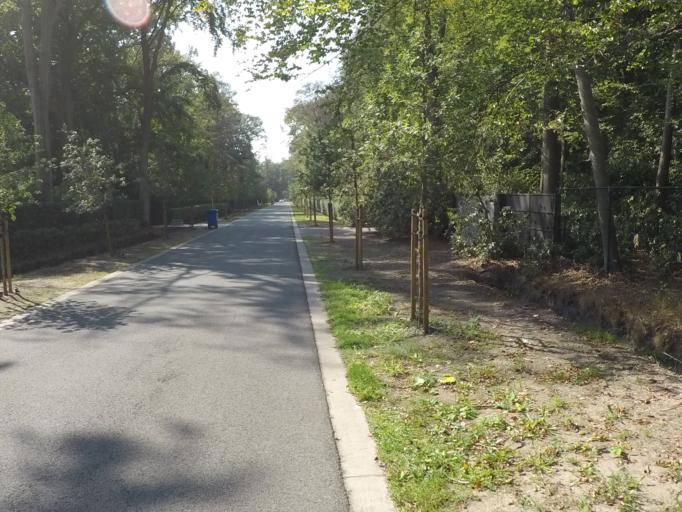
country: BE
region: Flanders
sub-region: Provincie Antwerpen
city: Kapellen
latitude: 51.3267
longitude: 4.4331
